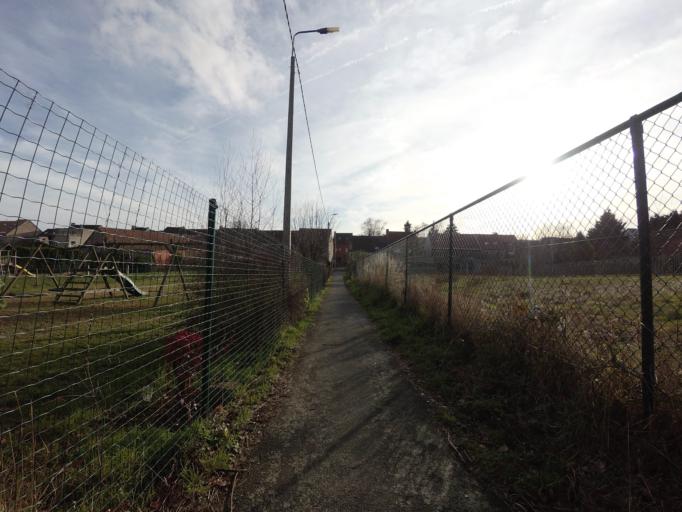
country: BE
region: Flanders
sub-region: Provincie Vlaams-Brabant
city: Kortenberg
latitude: 50.8795
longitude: 4.5505
